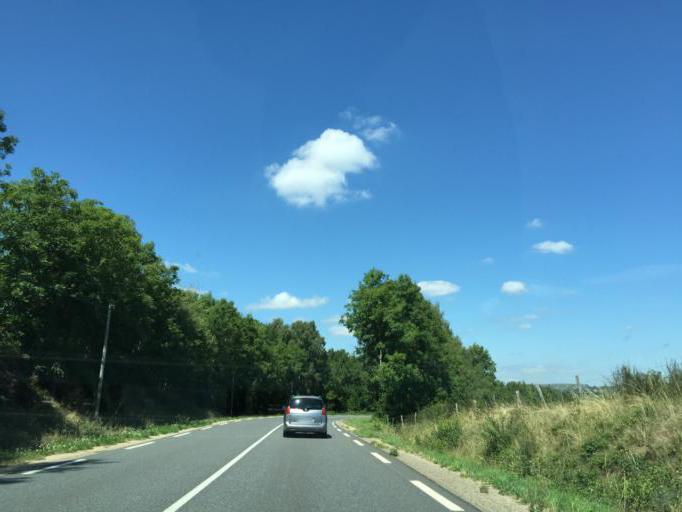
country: FR
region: Midi-Pyrenees
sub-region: Departement de l'Aveyron
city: Espalion
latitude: 44.6006
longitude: 2.7956
